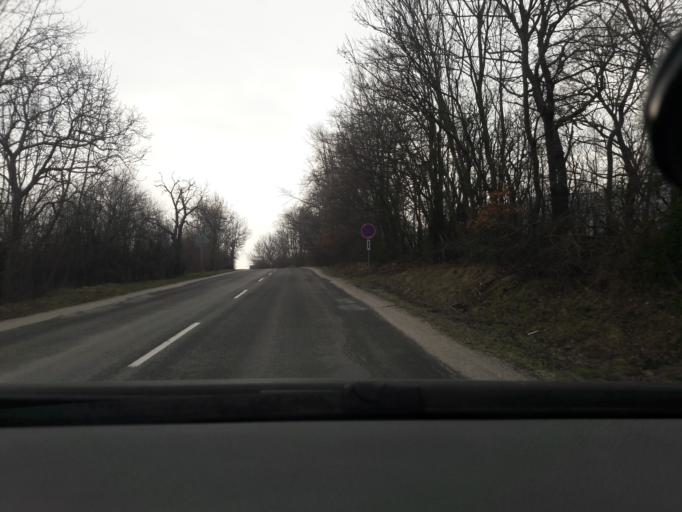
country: SK
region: Trnavsky
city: Smolenice
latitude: 48.4778
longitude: 17.4306
